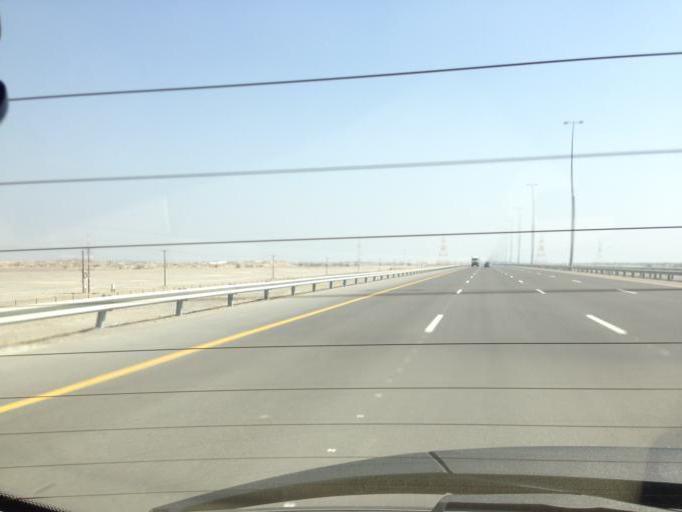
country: OM
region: Al Batinah
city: Barka'
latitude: 23.6047
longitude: 57.8219
